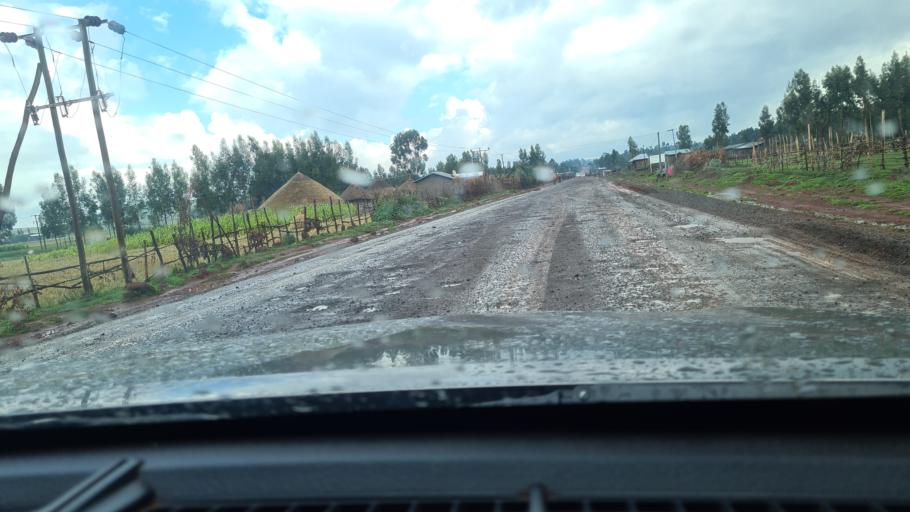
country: ET
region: Oromiya
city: Huruta
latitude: 8.0769
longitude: 39.5469
